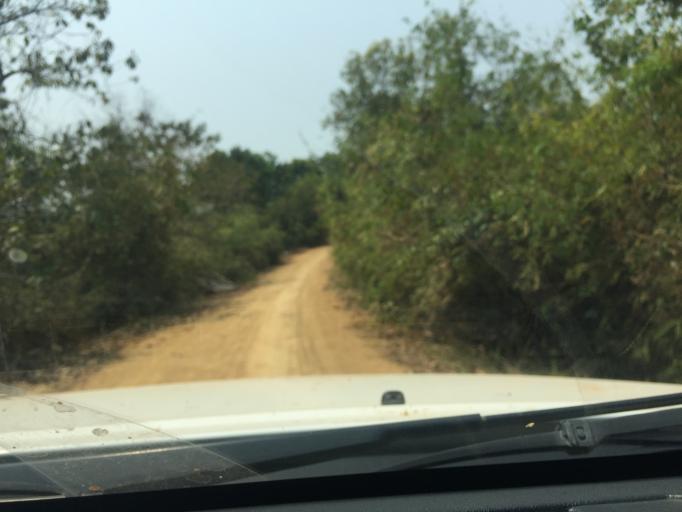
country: LA
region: Loungnamtha
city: Muang Nale
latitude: 20.6303
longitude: 101.6467
